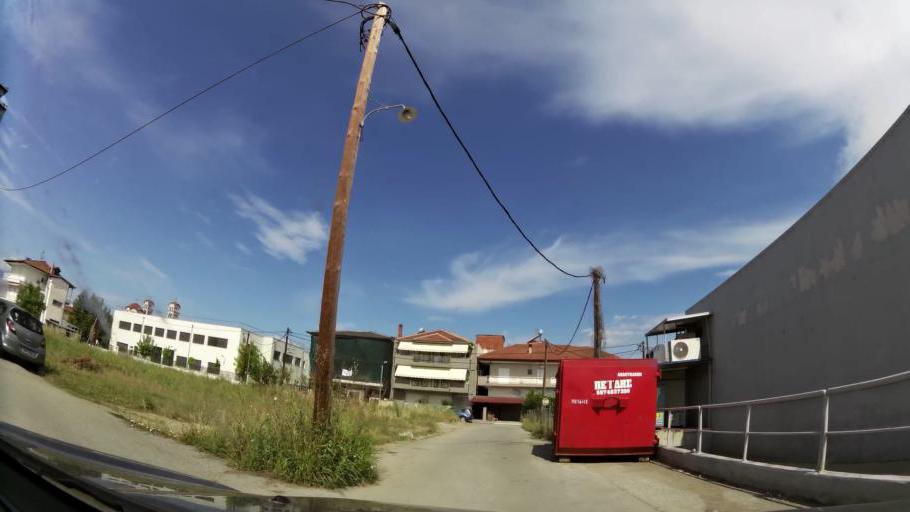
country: GR
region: Central Macedonia
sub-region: Nomos Pierias
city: Katerini
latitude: 40.2827
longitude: 22.5071
